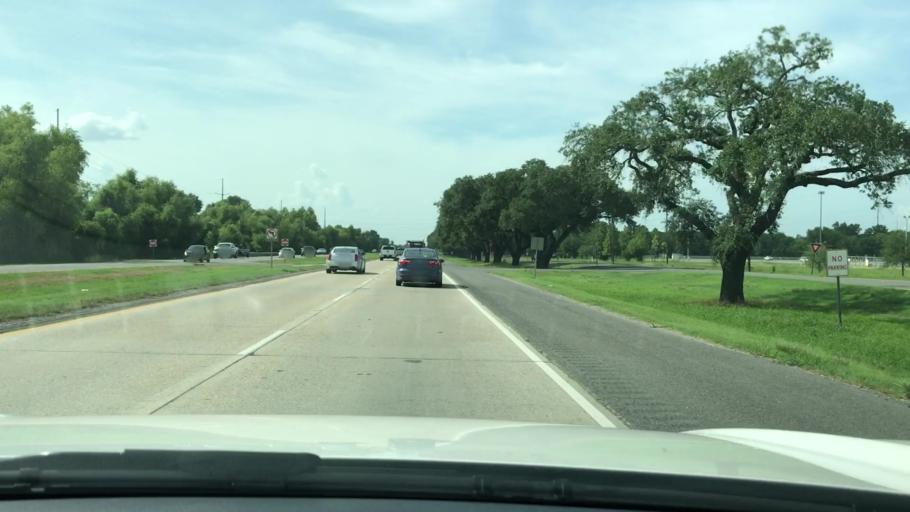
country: US
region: Louisiana
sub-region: West Baton Rouge Parish
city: Addis
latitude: 30.3245
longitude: -91.2534
